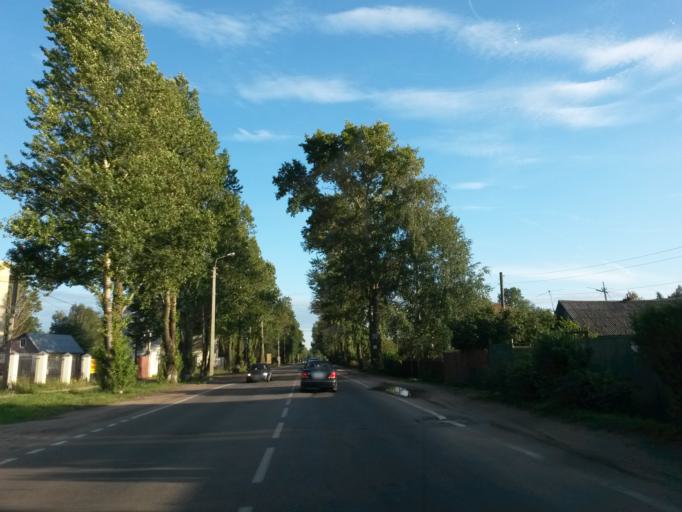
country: RU
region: Jaroslavl
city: Yaroslavl
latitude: 57.6647
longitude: 39.9092
